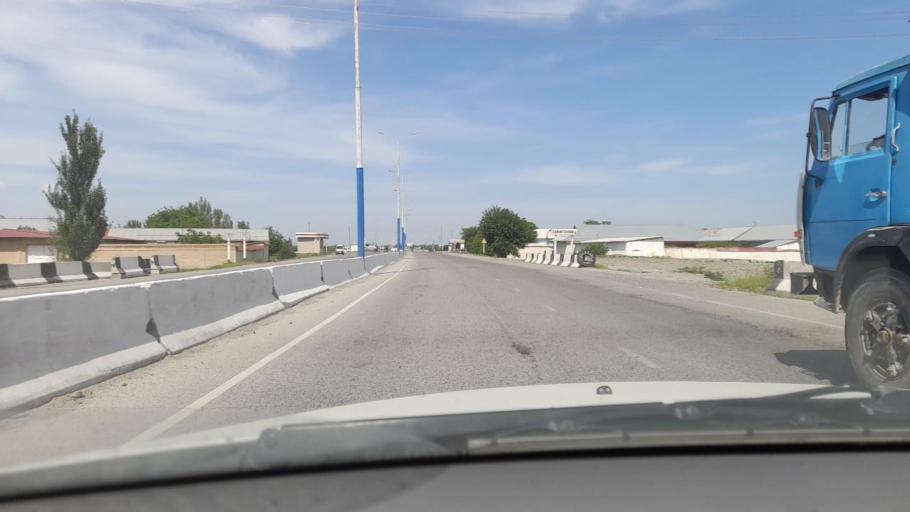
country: UZ
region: Samarqand
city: Kattaqo'rg'on
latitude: 39.9233
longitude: 66.3554
